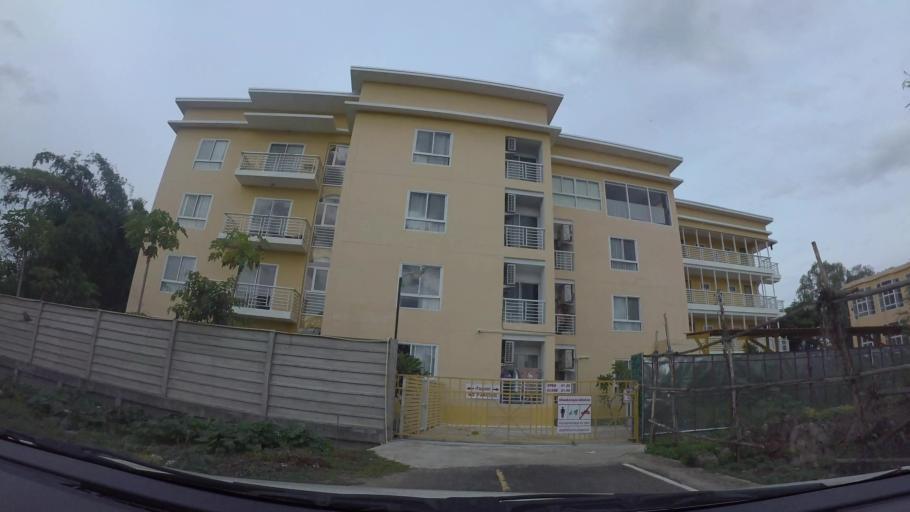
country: TH
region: Chiang Mai
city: Chiang Mai
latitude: 18.7428
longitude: 98.9711
